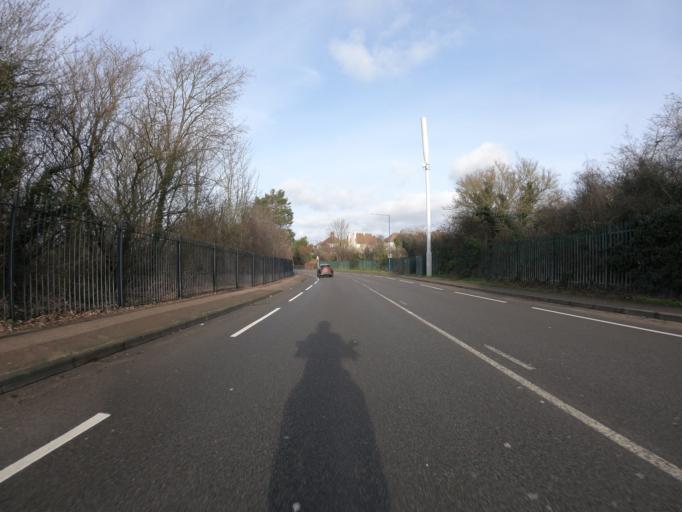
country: GB
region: England
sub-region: Kent
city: Gravesend
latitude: 51.4260
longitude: 0.3632
